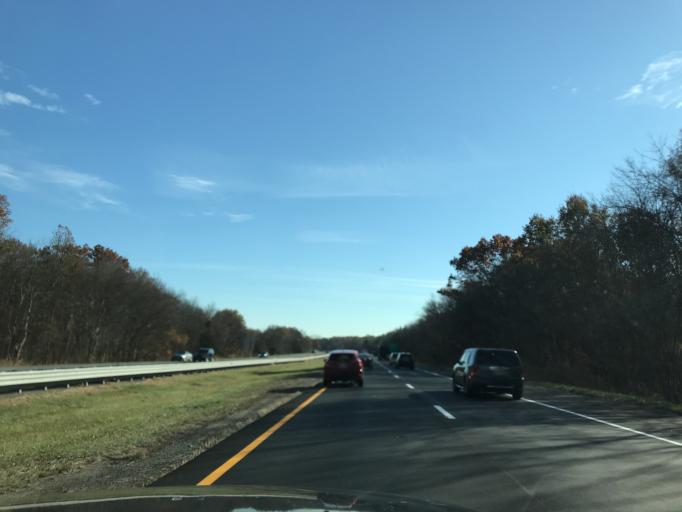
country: US
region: New Jersey
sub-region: Morris County
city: East Hanover
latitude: 40.8386
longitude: -74.3382
